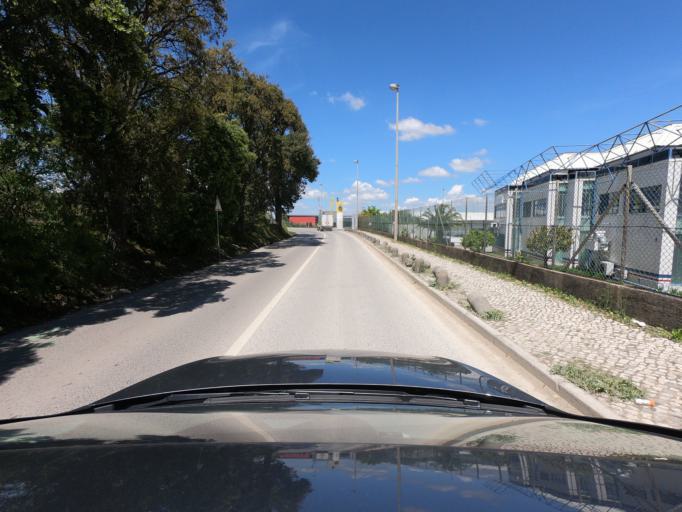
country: PT
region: Lisbon
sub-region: Amadora
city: Amadora
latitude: 38.7380
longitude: -9.2318
